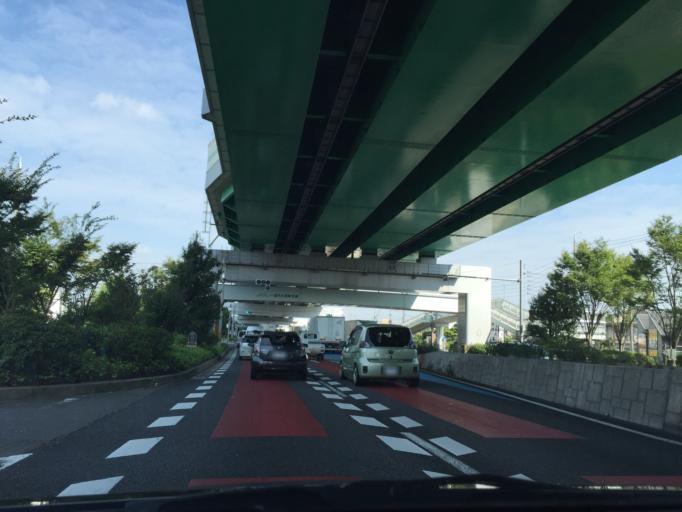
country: JP
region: Aichi
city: Ichinomiya
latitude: 35.2963
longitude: 136.7780
